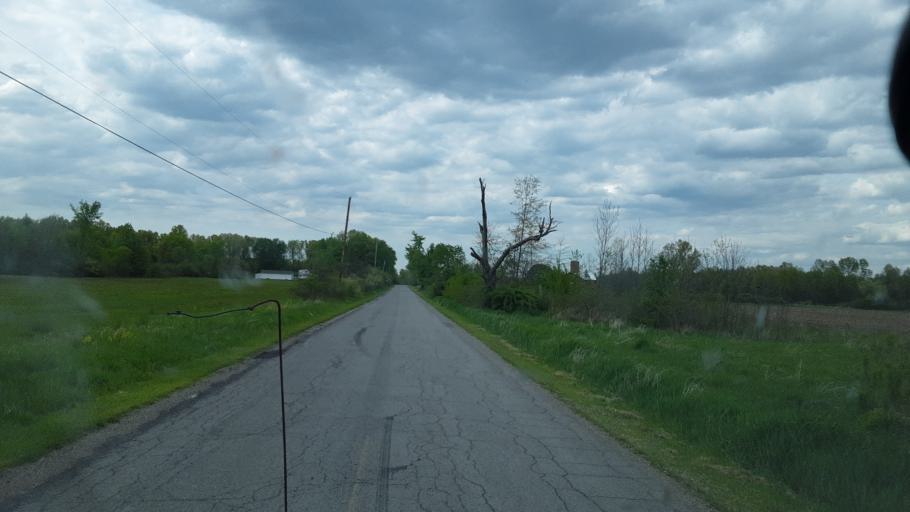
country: US
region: Ohio
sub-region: Portage County
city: Windham
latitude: 41.2838
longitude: -80.9836
